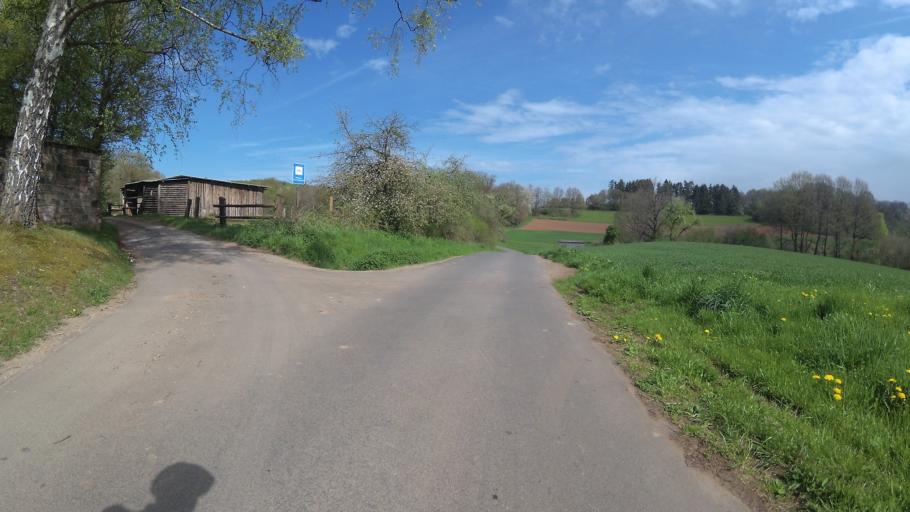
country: DE
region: Saarland
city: Mainzweiler
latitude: 49.4442
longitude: 7.1165
